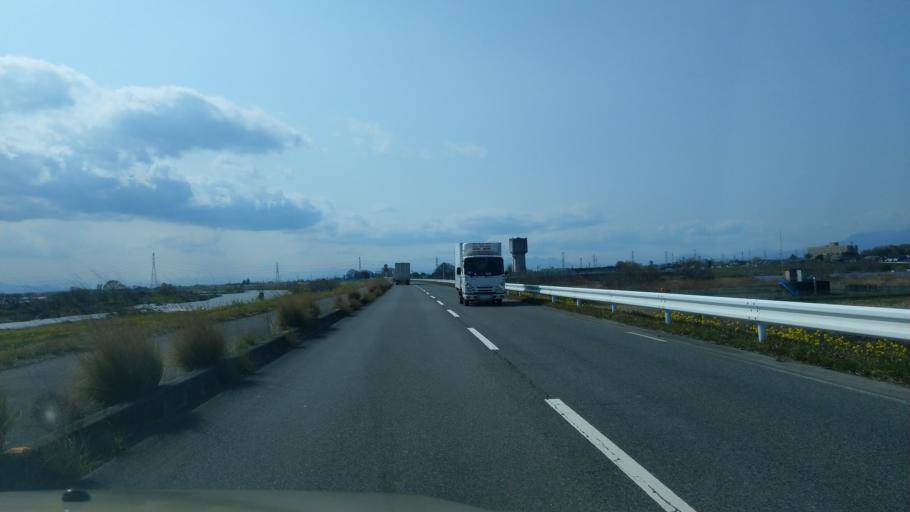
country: JP
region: Saitama
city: Menuma
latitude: 36.2440
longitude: 139.3756
